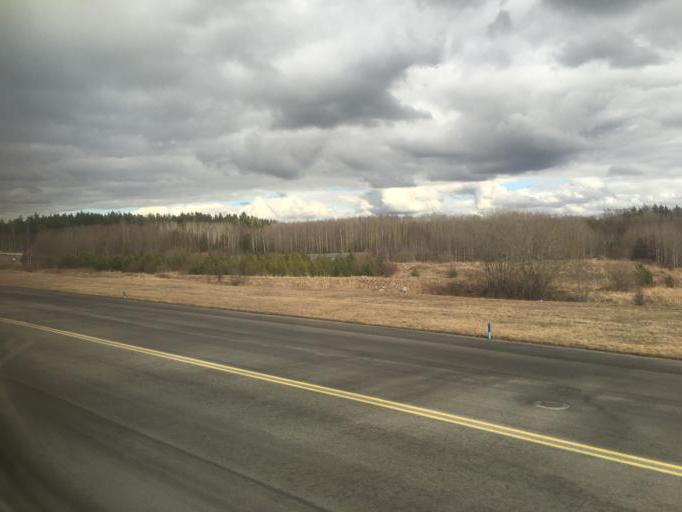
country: SE
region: Stockholm
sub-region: Sigtuna Kommun
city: Marsta
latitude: 59.6603
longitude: 17.9251
